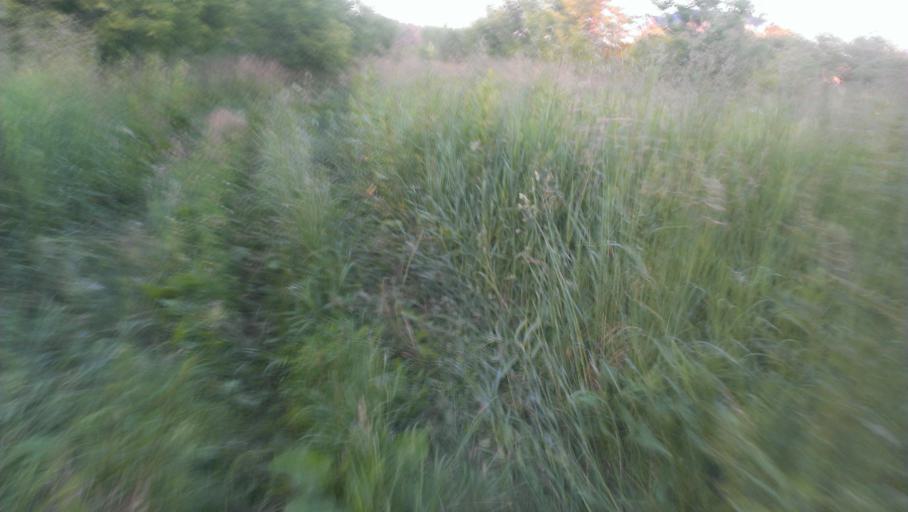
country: RU
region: Altai Krai
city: Novosilikatnyy
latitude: 53.3638
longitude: 83.6525
